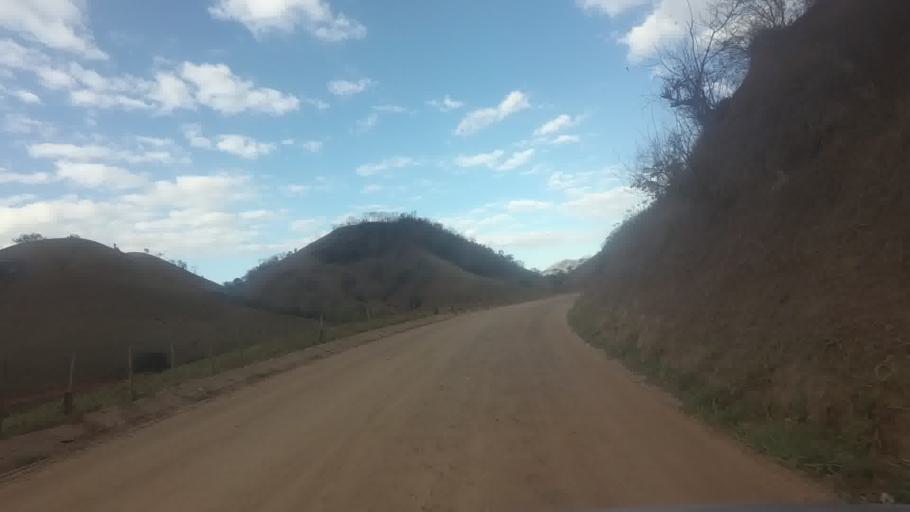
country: BR
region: Espirito Santo
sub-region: Mimoso Do Sul
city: Mimoso do Sul
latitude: -20.9467
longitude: -41.3626
